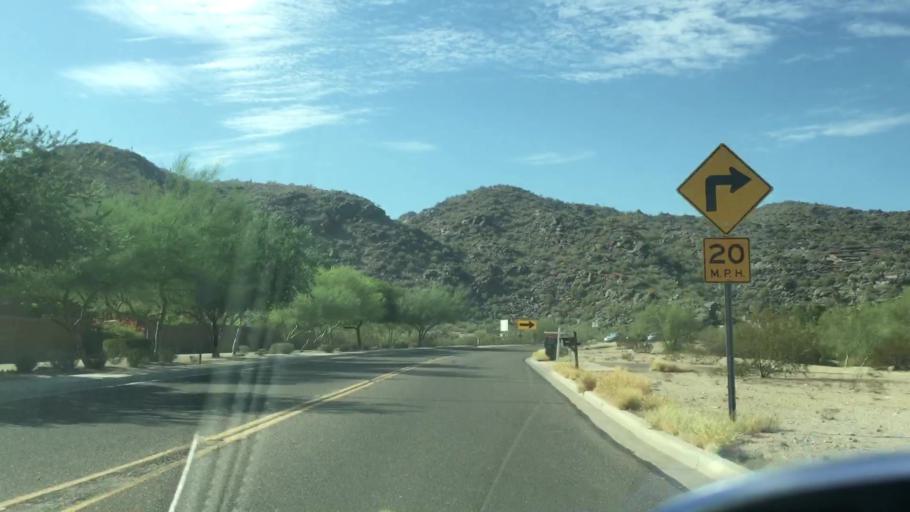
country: US
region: Arizona
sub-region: Maricopa County
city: Guadalupe
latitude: 33.3660
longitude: -112.0403
